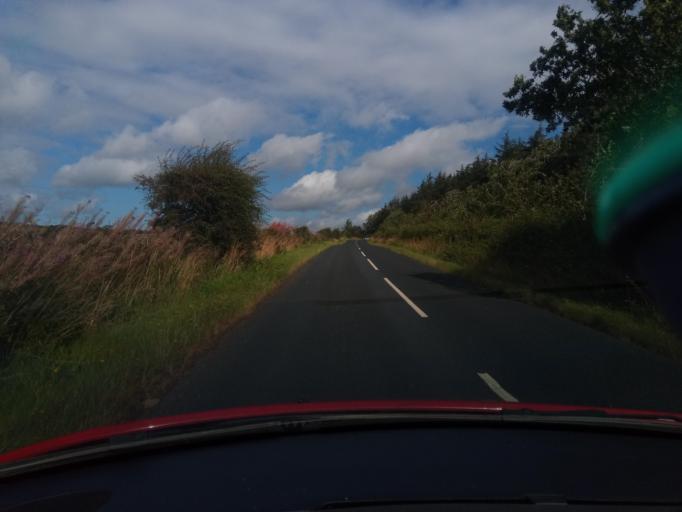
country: GB
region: Scotland
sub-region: The Scottish Borders
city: Melrose
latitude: 55.5723
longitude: -2.7320
